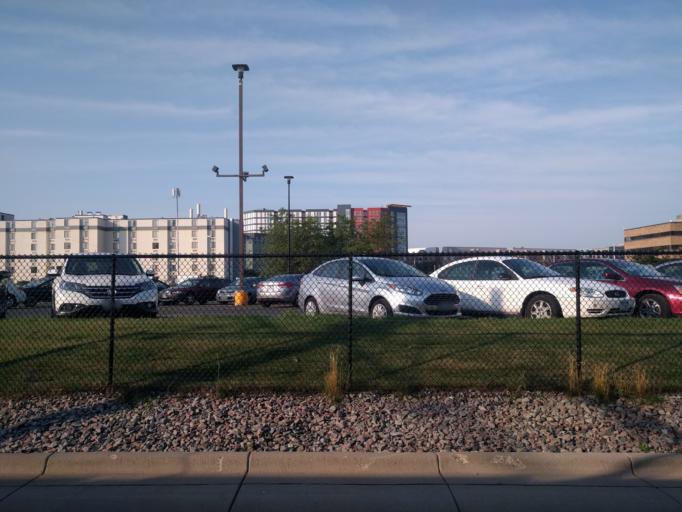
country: US
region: Minnesota
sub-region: Ramsey County
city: Lauderdale
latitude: 44.9755
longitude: -93.2215
